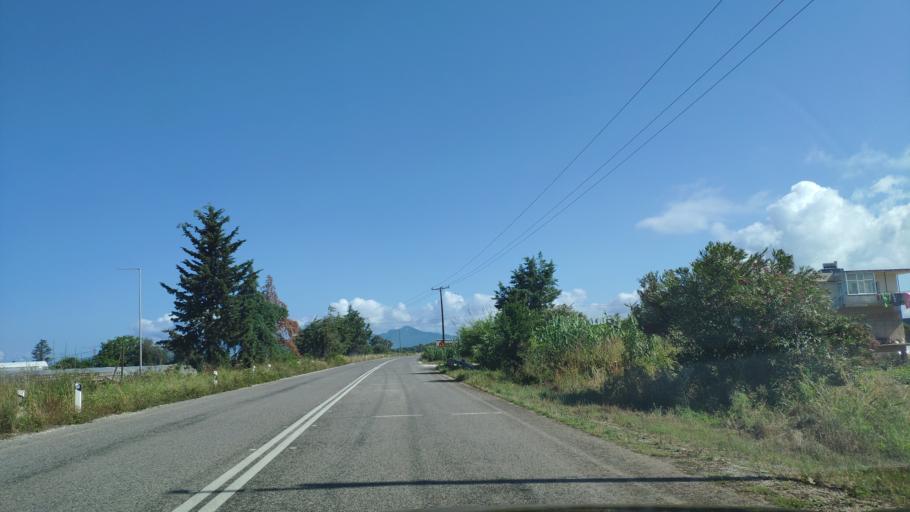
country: GR
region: Epirus
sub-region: Nomos Prevezis
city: Preveza
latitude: 38.9872
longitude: 20.7140
